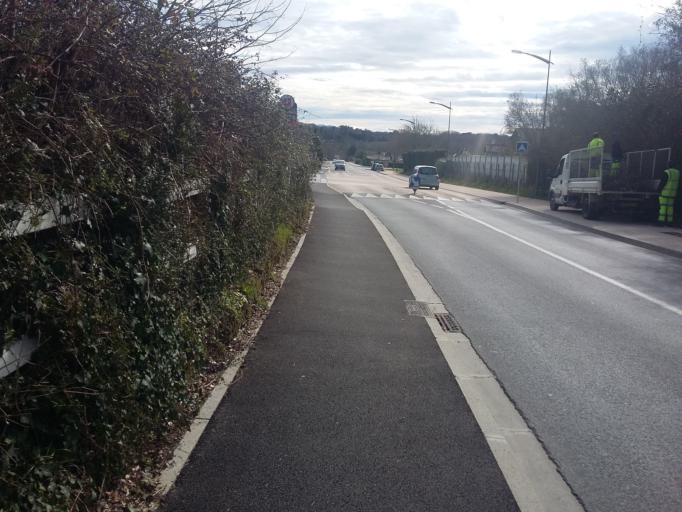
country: FR
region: Aquitaine
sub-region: Departement des Landes
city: Saint-Martin-de-Seignanx
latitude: 43.5430
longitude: -1.3872
